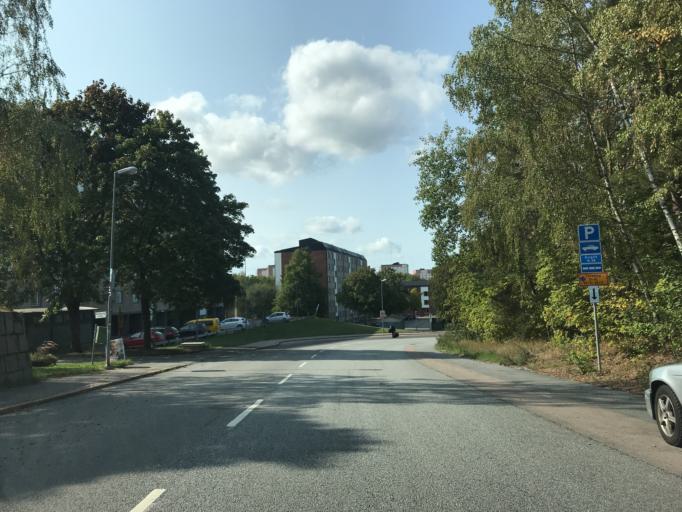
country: SE
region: Stockholm
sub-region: Sollentuna Kommun
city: Sollentuna
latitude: 59.4477
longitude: 17.9726
